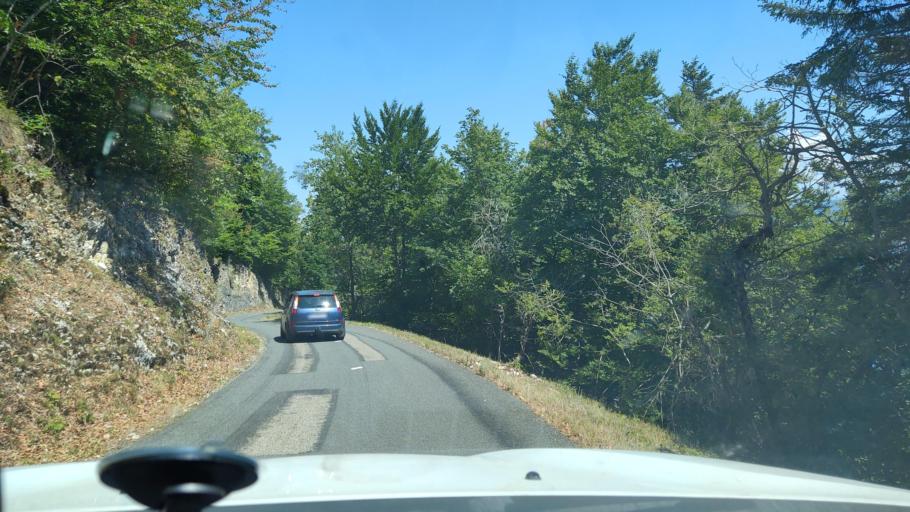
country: FR
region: Rhone-Alpes
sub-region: Departement de la Savoie
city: Le Bourget-du-Lac
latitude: 45.6514
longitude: 5.8284
